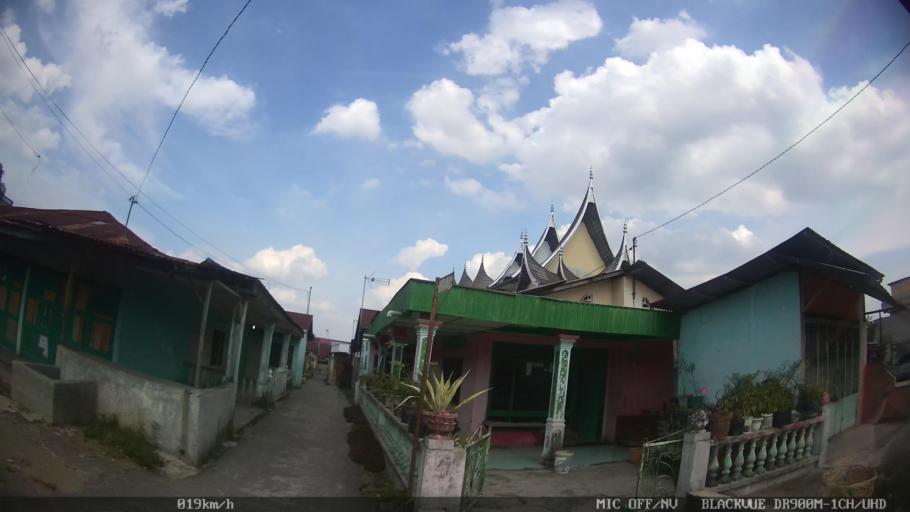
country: ID
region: North Sumatra
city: Binjai
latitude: 3.6145
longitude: 98.4992
